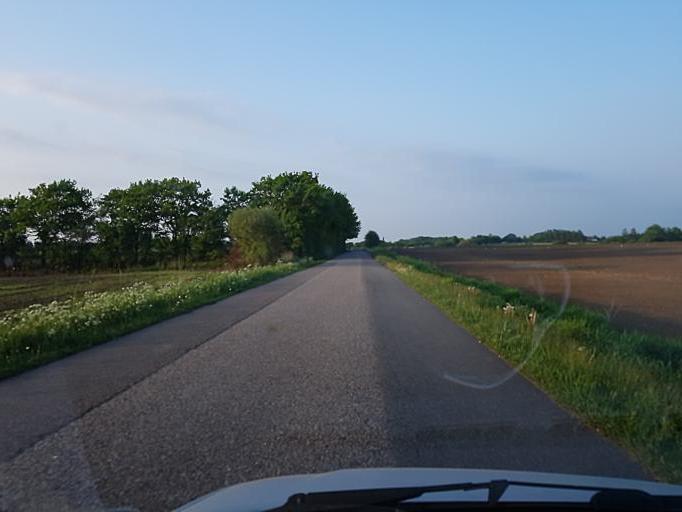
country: DK
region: South Denmark
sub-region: Esbjerg Kommune
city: Tjaereborg
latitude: 55.5544
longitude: 8.5493
